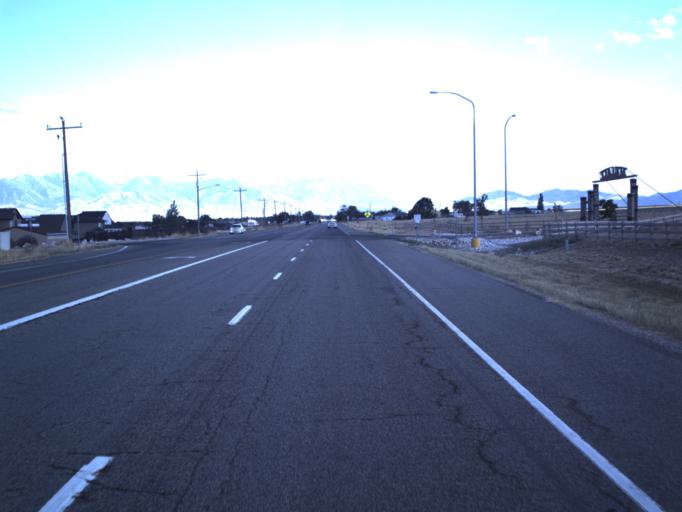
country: US
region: Utah
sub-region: Tooele County
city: Grantsville
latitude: 40.6201
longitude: -112.5027
